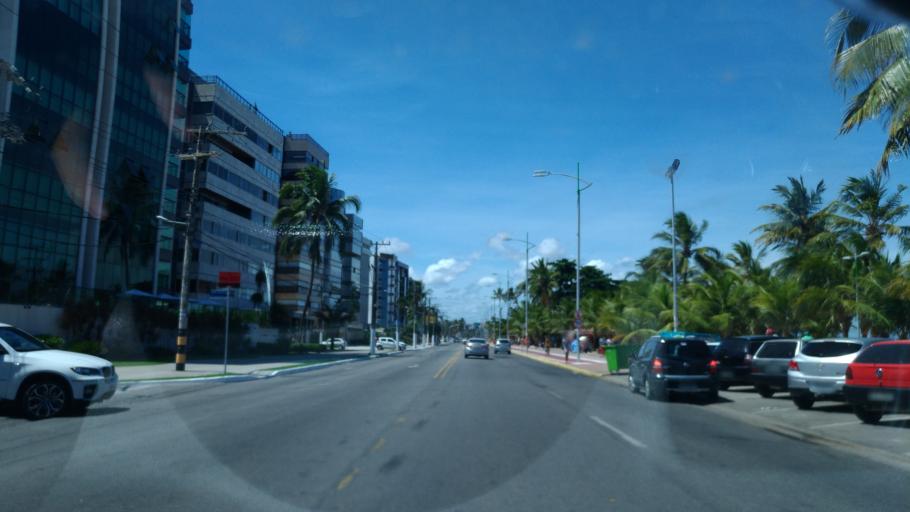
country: BR
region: Alagoas
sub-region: Maceio
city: Maceio
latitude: -9.6559
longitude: -35.6986
